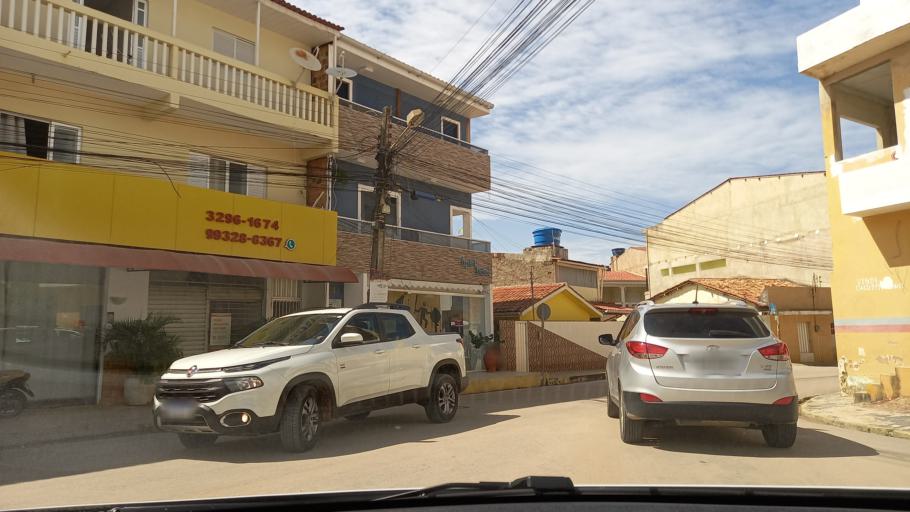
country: BR
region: Alagoas
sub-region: Maragogi
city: Maragogi
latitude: -9.0076
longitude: -35.2180
